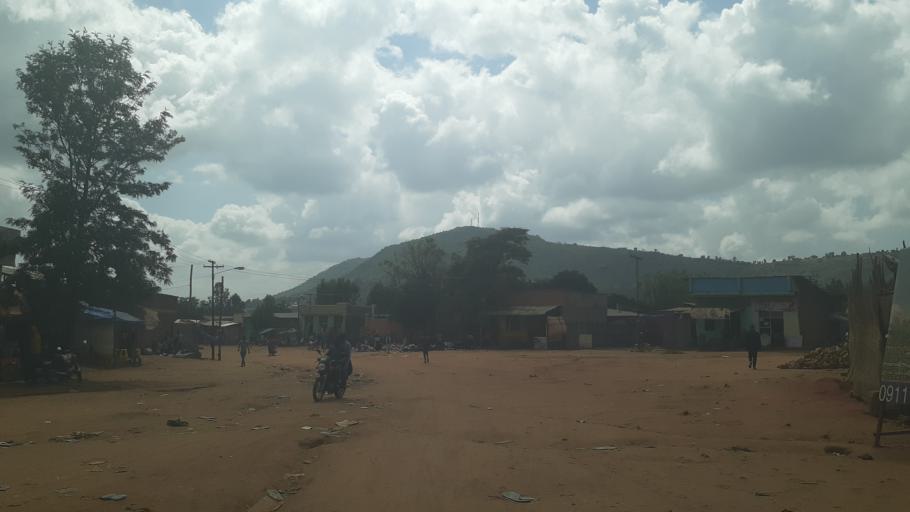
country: ET
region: Oromiya
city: Yabelo
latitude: 4.8969
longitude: 38.0904
